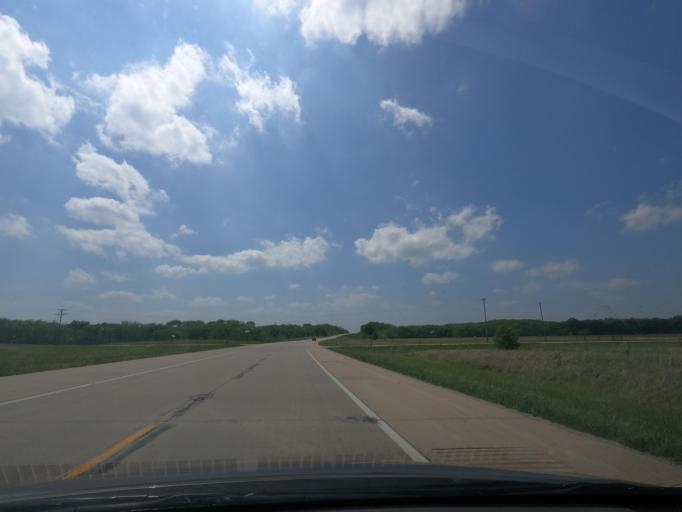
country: US
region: Kansas
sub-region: Wilson County
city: Fredonia
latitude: 37.6184
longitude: -95.9969
